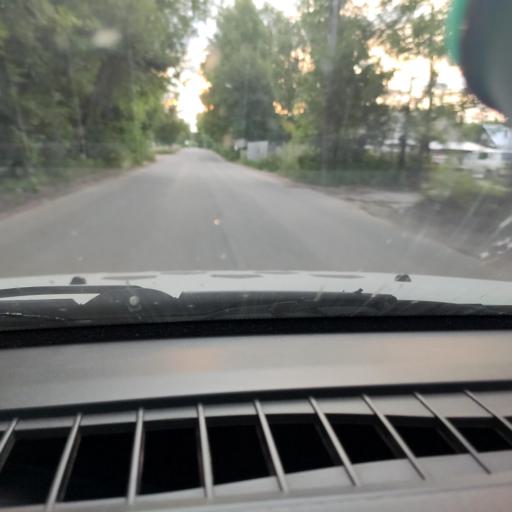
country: RU
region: Kirov
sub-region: Kirovo-Chepetskiy Rayon
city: Kirov
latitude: 58.6176
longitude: 49.6063
